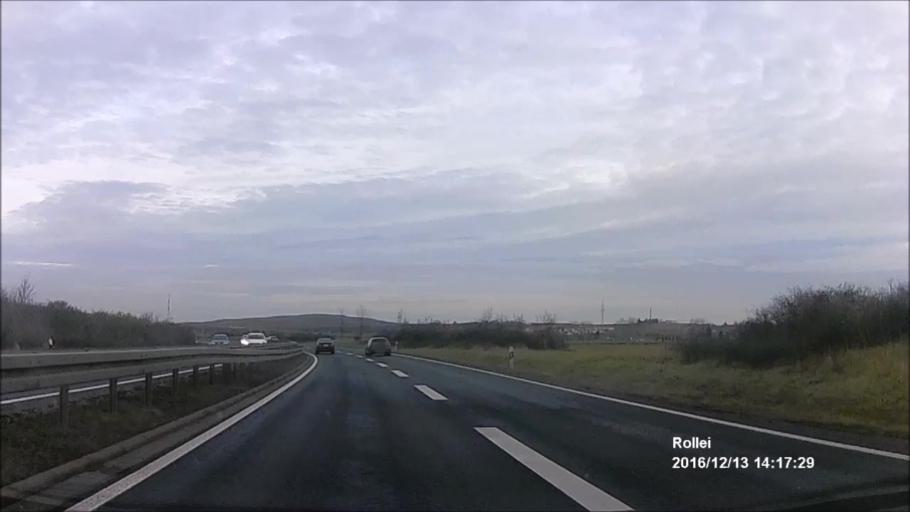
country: DE
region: Thuringia
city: Kleinmolsen
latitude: 51.0318
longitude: 11.0638
